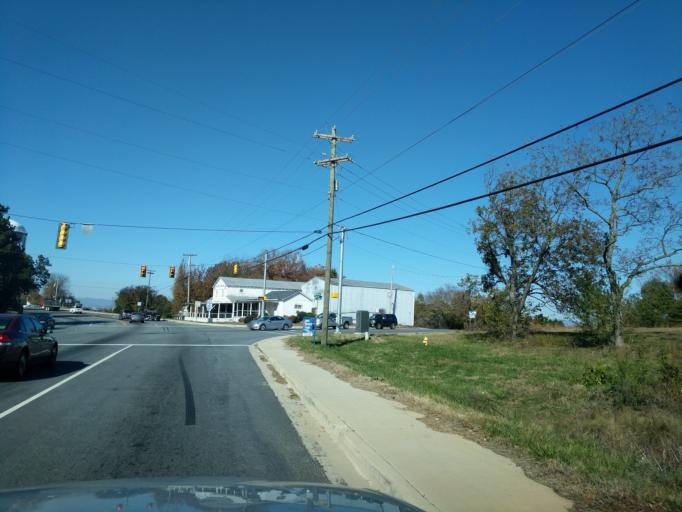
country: US
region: South Carolina
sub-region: Greenville County
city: Greer
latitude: 34.9470
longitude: -82.2615
